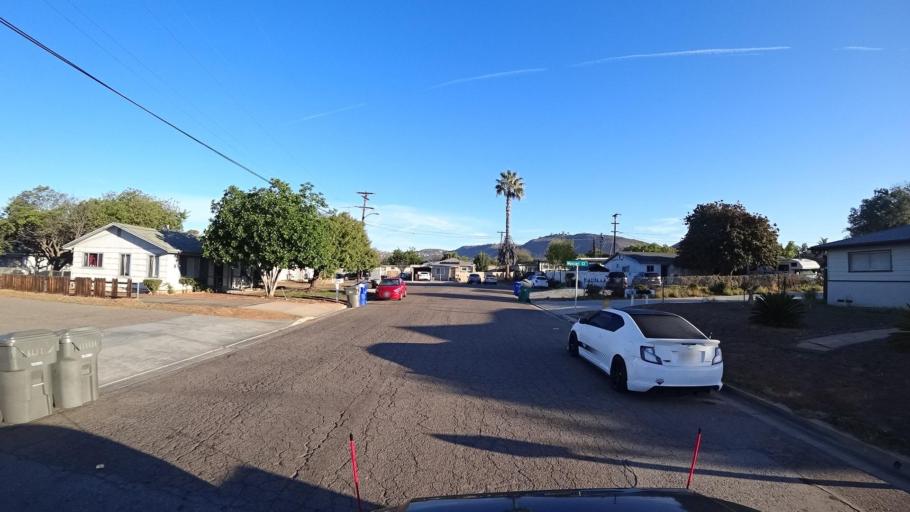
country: US
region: California
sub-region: San Diego County
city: Bostonia
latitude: 32.8110
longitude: -116.9481
